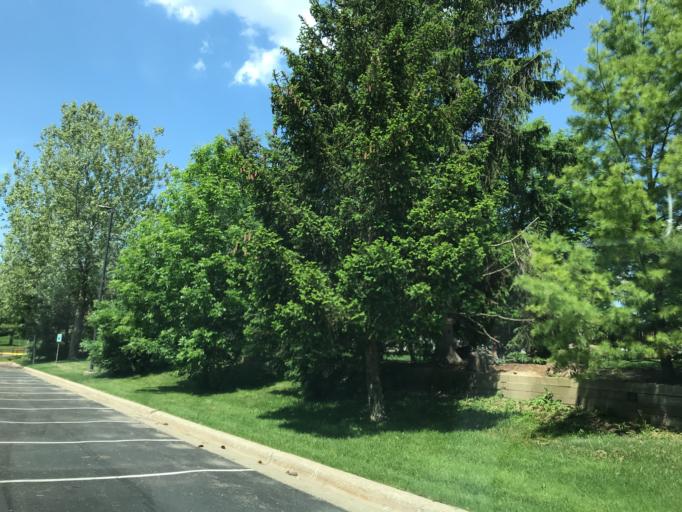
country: US
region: Michigan
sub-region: Washtenaw County
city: Ann Arbor
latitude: 42.2549
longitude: -83.7191
